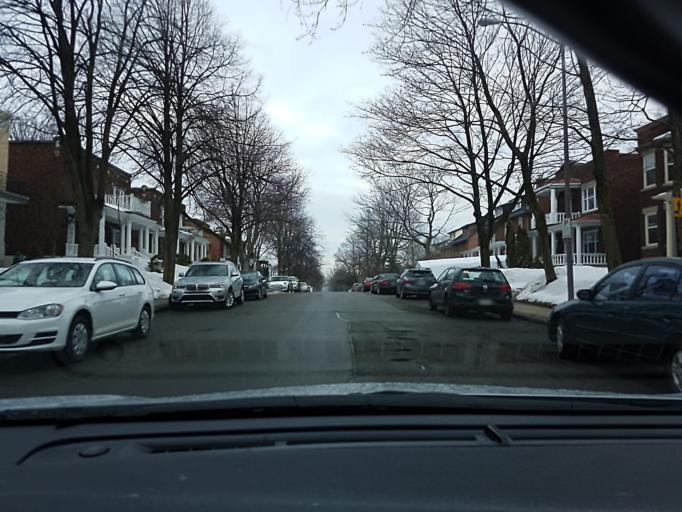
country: CA
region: Quebec
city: Quebec
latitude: 46.7974
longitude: -71.2344
